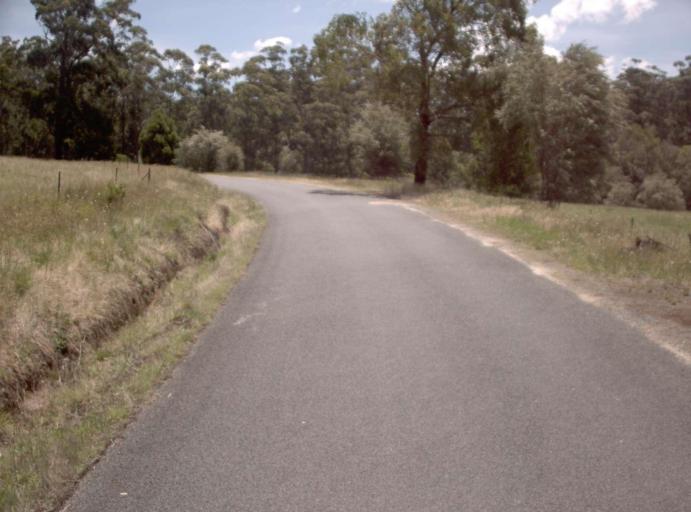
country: AU
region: New South Wales
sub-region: Bombala
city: Bombala
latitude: -37.5210
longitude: 148.9322
